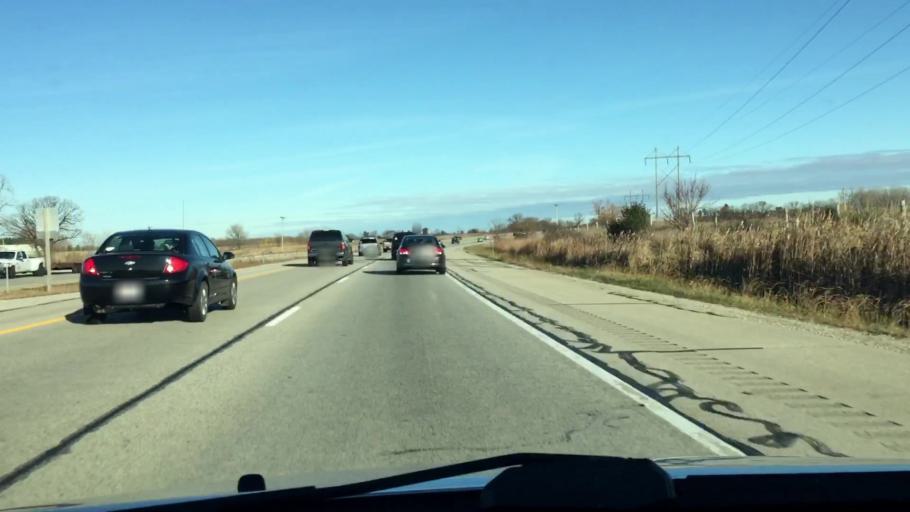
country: US
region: Wisconsin
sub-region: Fond du Lac County
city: Rosendale
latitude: 43.8596
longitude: -88.5823
